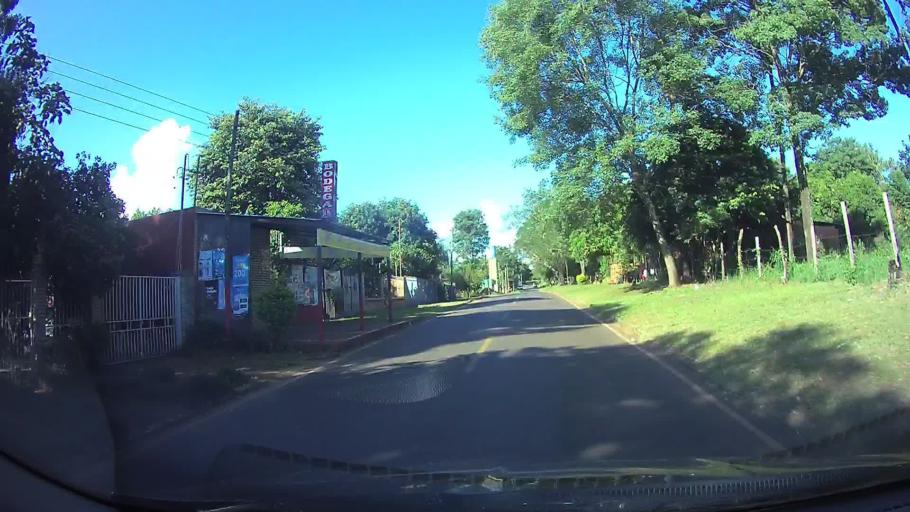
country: PY
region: Central
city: Aregua
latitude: -25.3510
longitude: -57.3935
